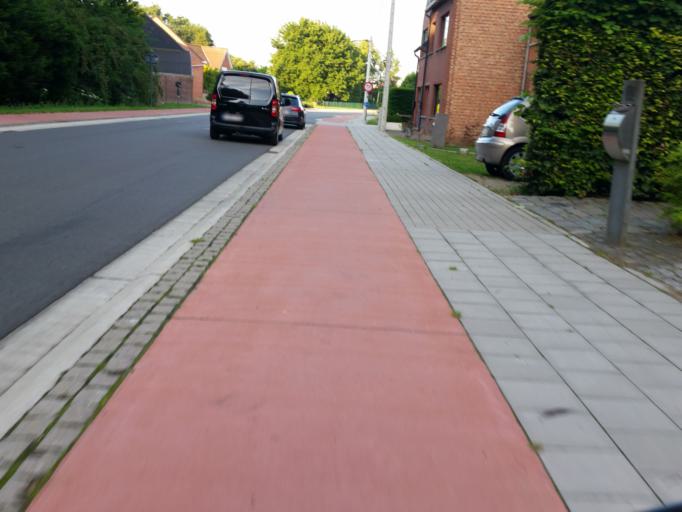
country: BE
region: Flanders
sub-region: Provincie Vlaams-Brabant
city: Zemst
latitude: 50.9786
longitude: 4.4406
